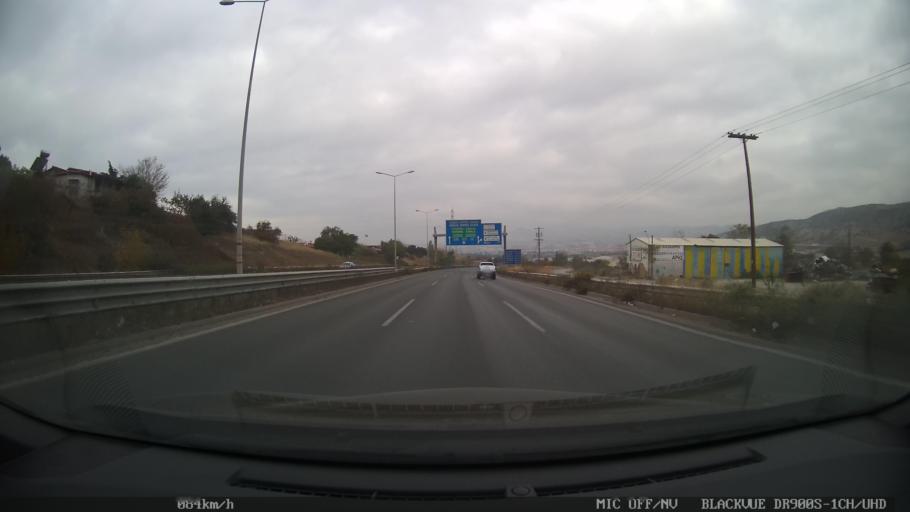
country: GR
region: Central Macedonia
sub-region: Nomos Thessalonikis
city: Polichni
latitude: 40.6646
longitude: 22.9652
